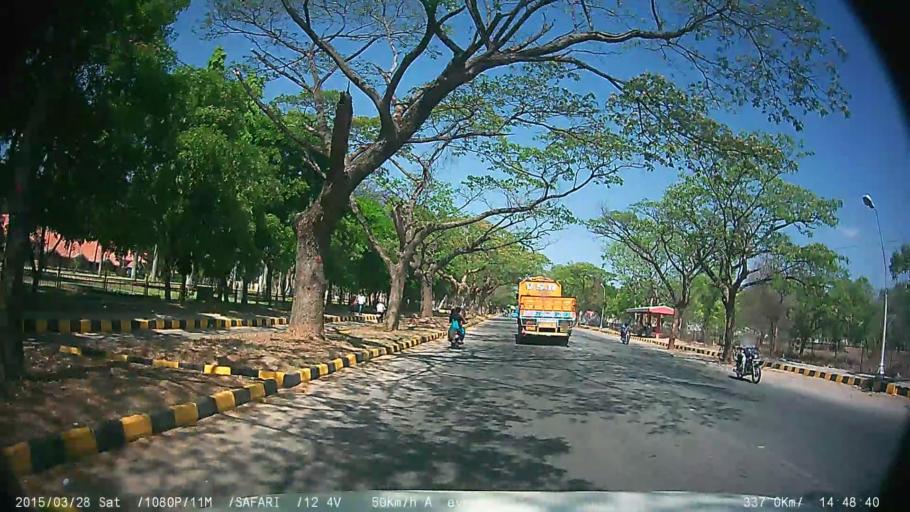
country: IN
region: Karnataka
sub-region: Mysore
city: Mysore
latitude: 12.2981
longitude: 76.6733
